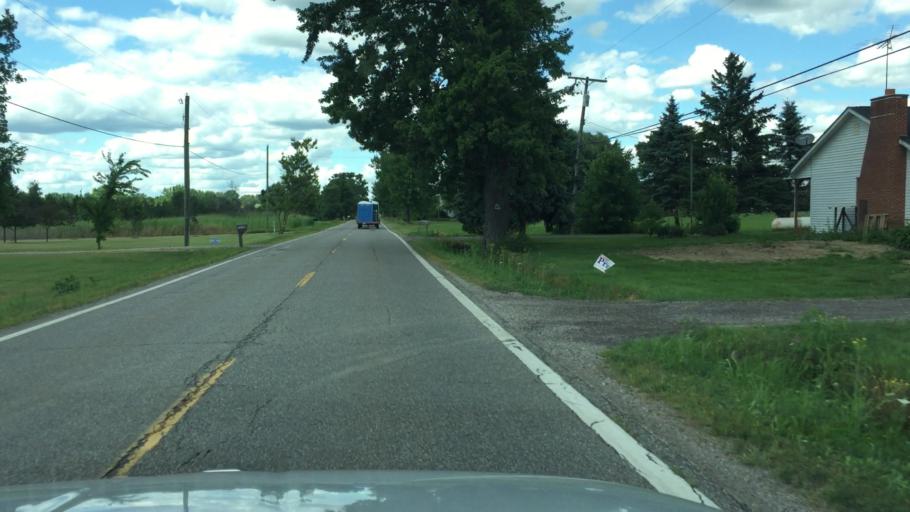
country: US
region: Michigan
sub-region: Macomb County
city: Armada
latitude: 42.8797
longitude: -82.9454
